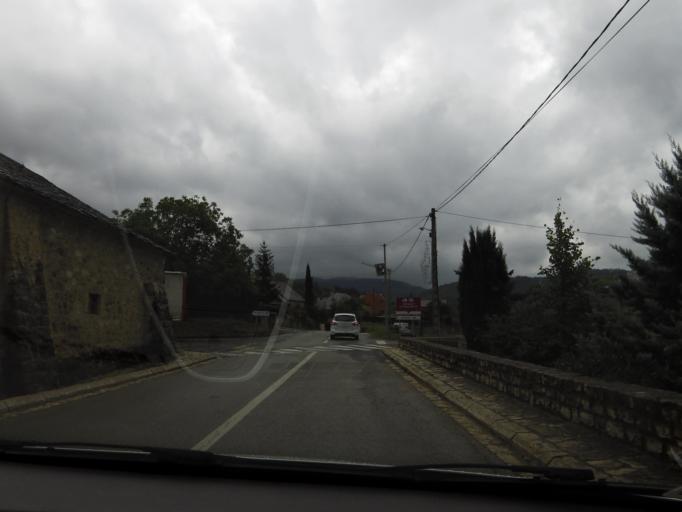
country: FR
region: Languedoc-Roussillon
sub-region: Departement de la Lozere
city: Florac
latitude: 44.3768
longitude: 3.5240
